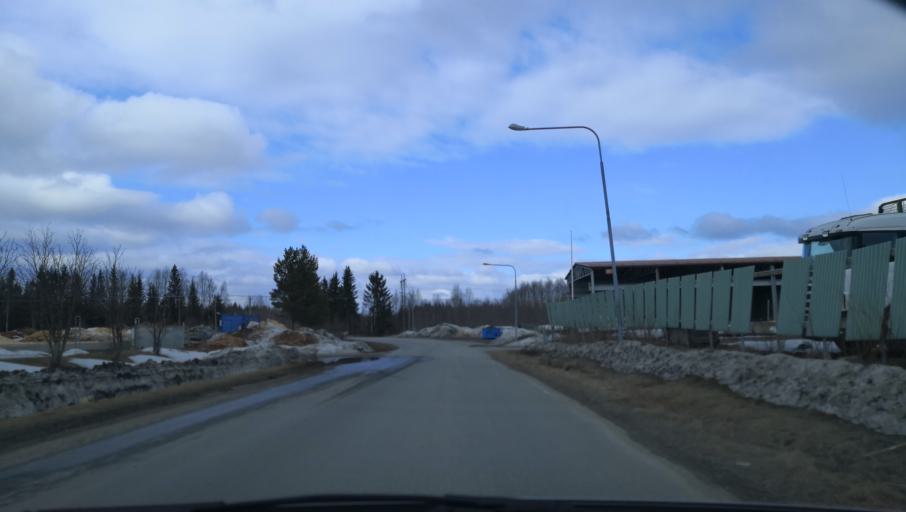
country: SE
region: Vaesterbotten
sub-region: Vannas Kommun
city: Vaennaes
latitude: 63.9160
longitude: 19.7434
